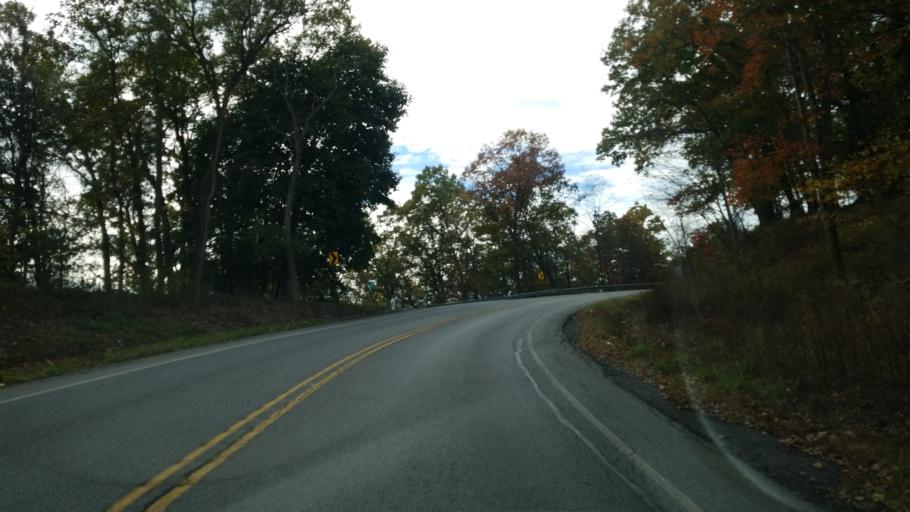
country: US
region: Pennsylvania
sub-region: Clearfield County
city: Clearfield
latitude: 41.0421
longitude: -78.3831
